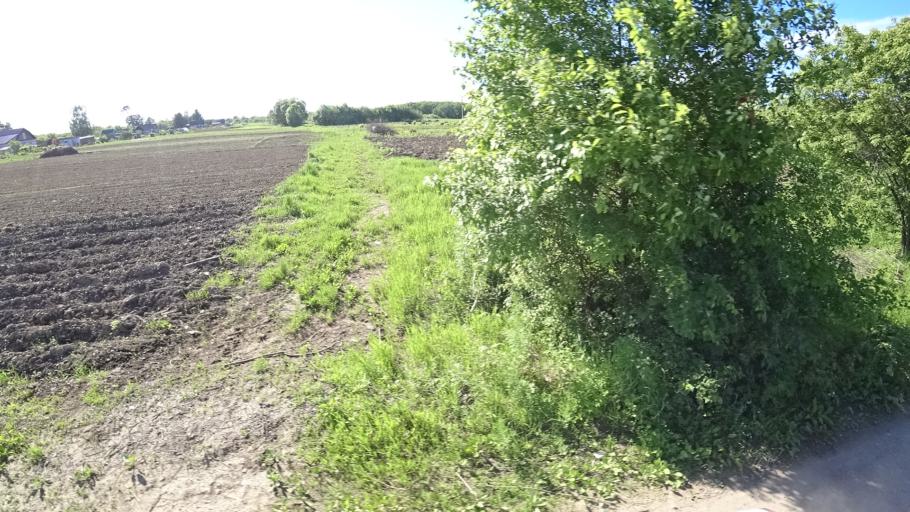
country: RU
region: Khabarovsk Krai
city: Khor
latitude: 47.8863
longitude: 135.0191
